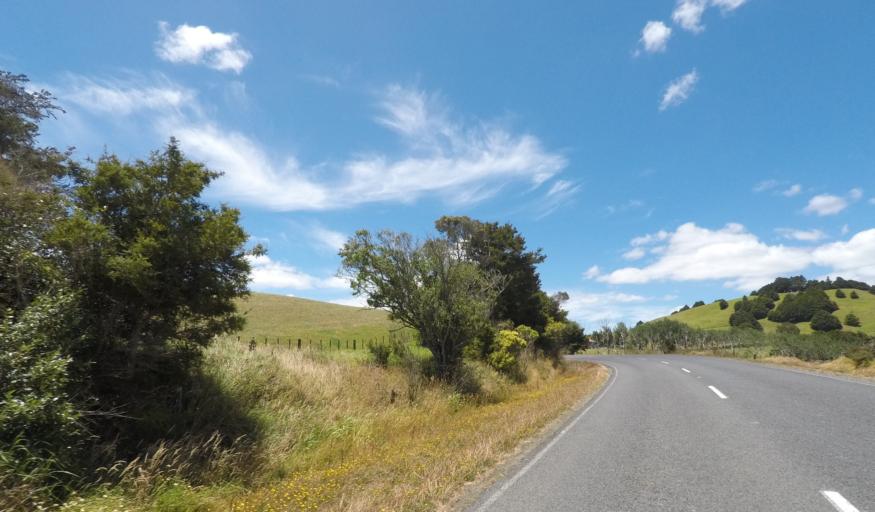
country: NZ
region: Northland
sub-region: Whangarei
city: Whangarei
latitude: -35.5600
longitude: 174.2896
